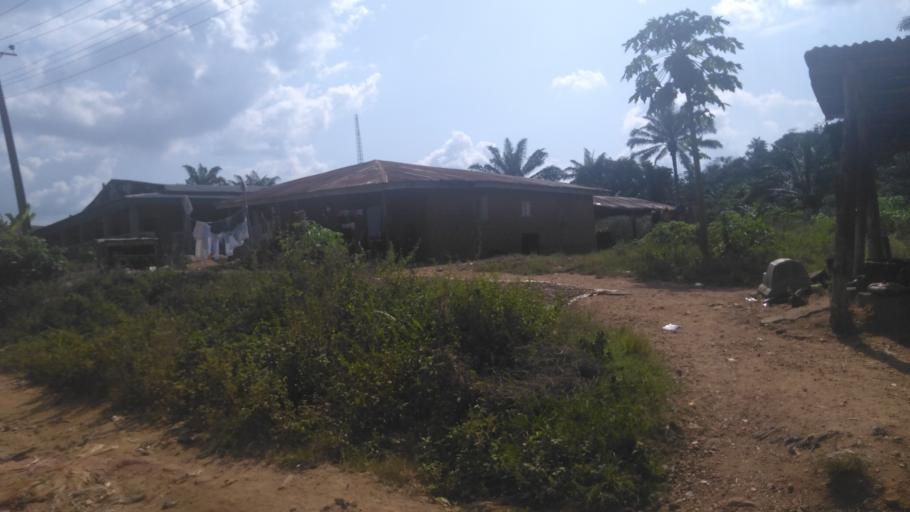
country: NG
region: Osun
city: Ifetedo
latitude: 7.0227
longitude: 4.6308
